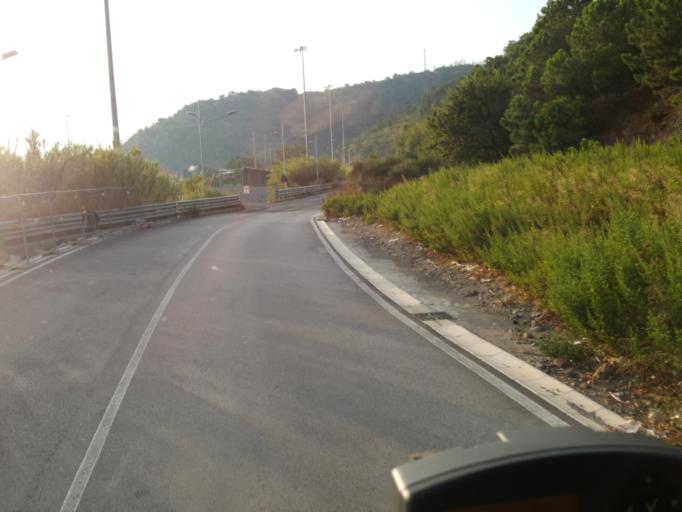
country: IT
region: Liguria
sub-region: Provincia di Savona
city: Vado Ligure
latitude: 44.2649
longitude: 8.4398
